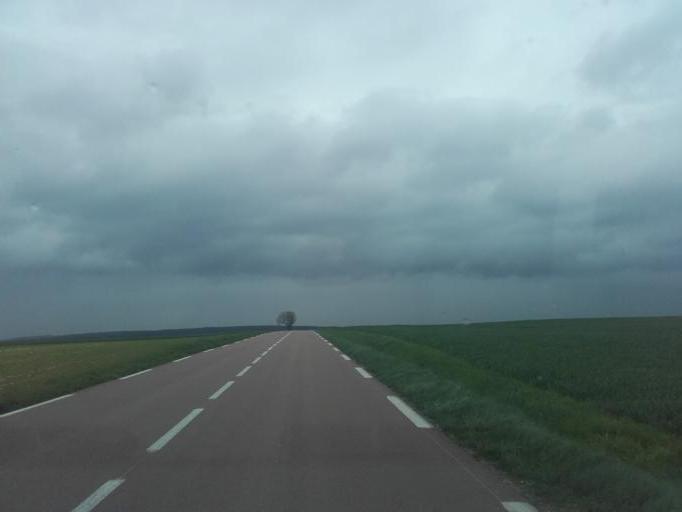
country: FR
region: Bourgogne
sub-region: Departement de l'Yonne
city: Joux-la-Ville
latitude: 47.7143
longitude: 3.8526
